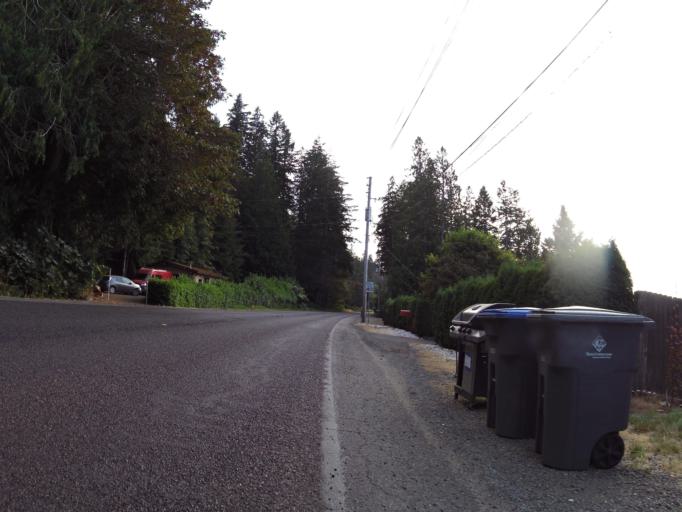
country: US
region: Washington
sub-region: Mason County
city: Allyn
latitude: 47.3937
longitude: -122.9042
